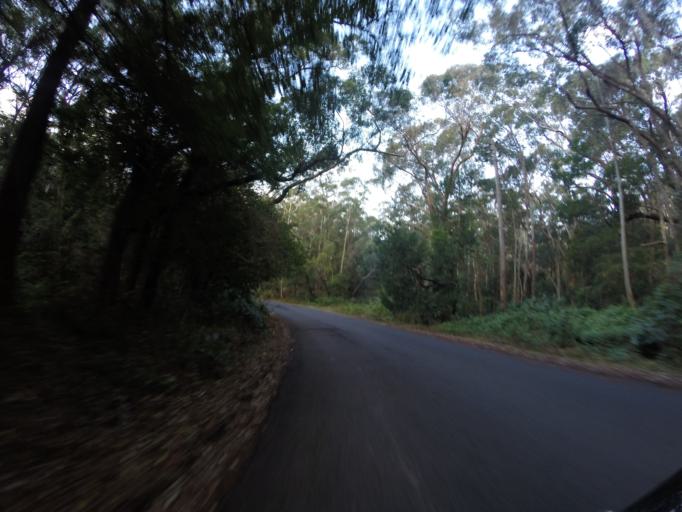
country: AU
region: New South Wales
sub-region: Wollongong
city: Cordeaux Heights
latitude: -34.4335
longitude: 150.8051
